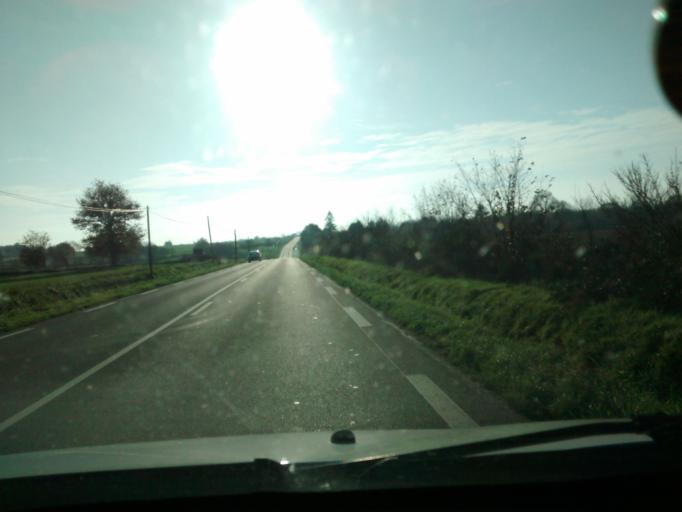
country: FR
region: Brittany
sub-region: Departement d'Ille-et-Vilaine
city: Tremblay
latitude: 48.4131
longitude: -1.4782
